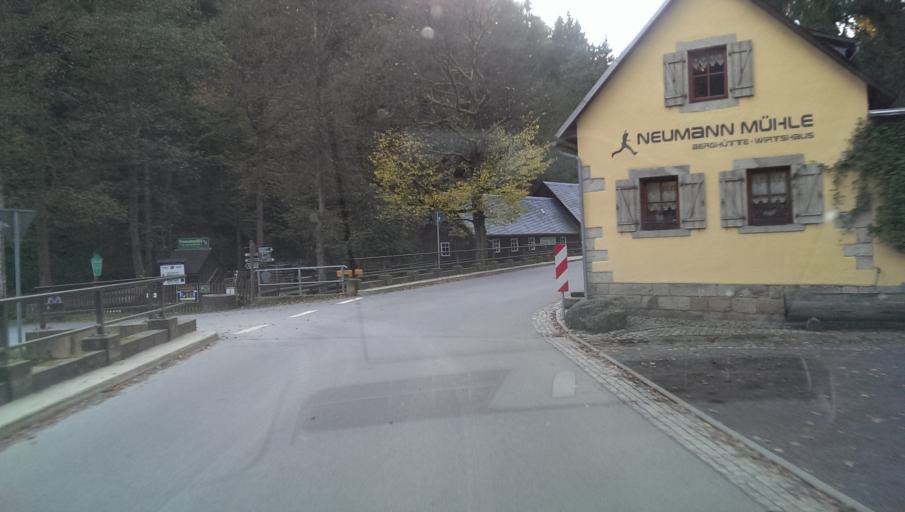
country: DE
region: Saxony
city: Sebnitz
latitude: 50.9236
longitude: 14.2848
